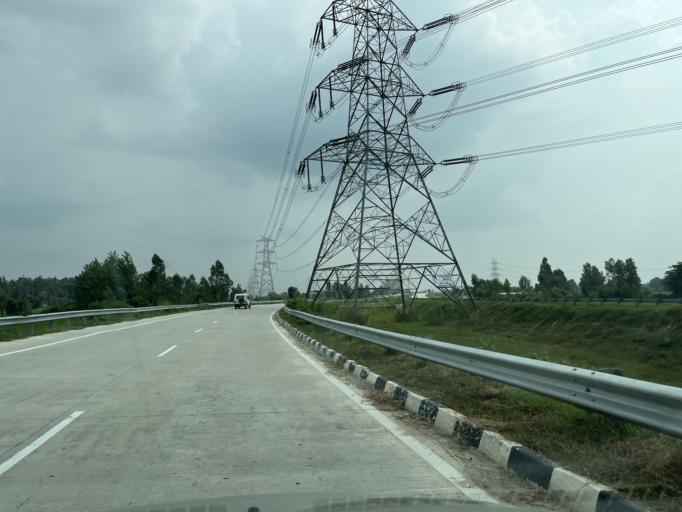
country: IN
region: Uttarakhand
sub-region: Udham Singh Nagar
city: Jaspur
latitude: 29.2781
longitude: 78.8679
